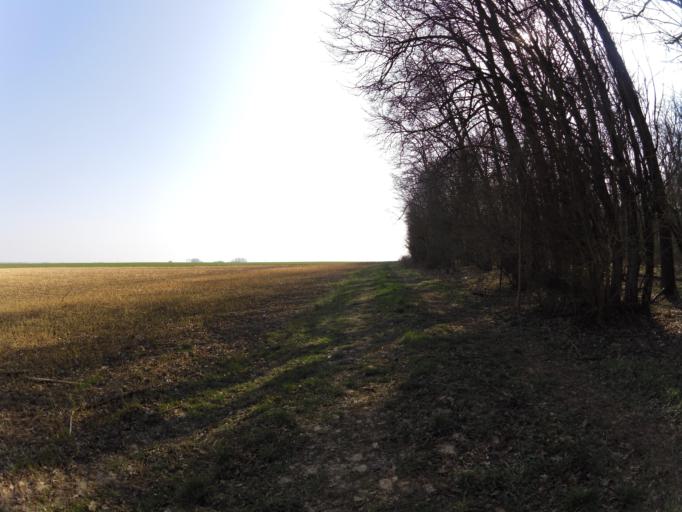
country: DE
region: Bavaria
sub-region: Regierungsbezirk Unterfranken
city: Geroldshausen
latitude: 49.6732
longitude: 9.9127
